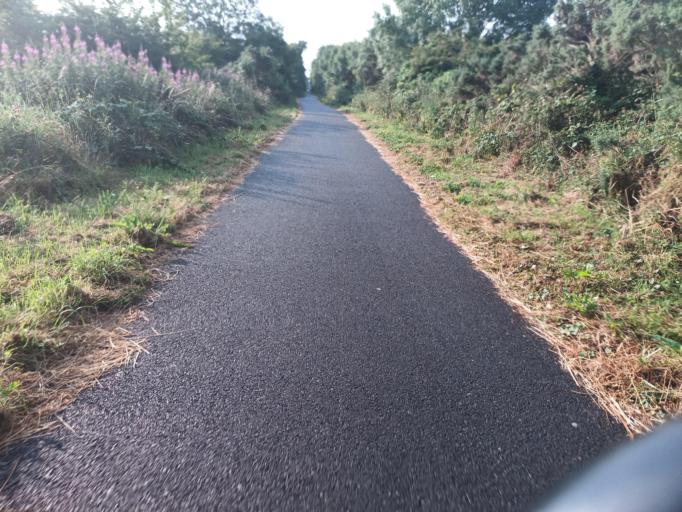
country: GB
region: Northern Ireland
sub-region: Castlereagh District
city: Dundonald
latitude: 54.5742
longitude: -5.7778
